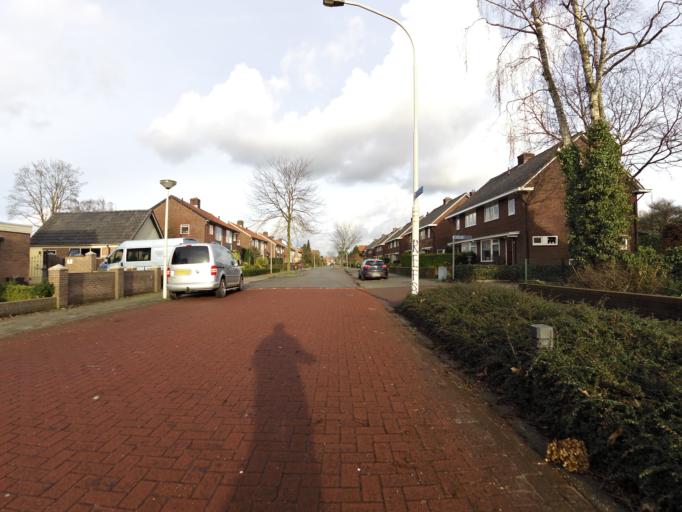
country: NL
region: Gelderland
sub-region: Gemeente Doetinchem
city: Doetinchem
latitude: 51.9605
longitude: 6.3074
